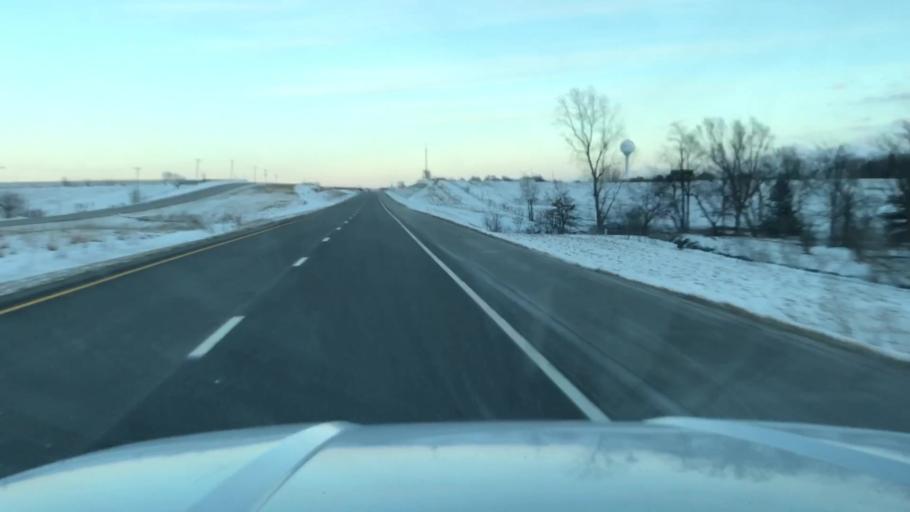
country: US
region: Missouri
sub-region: Clinton County
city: Gower
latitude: 39.7620
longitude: -94.5140
